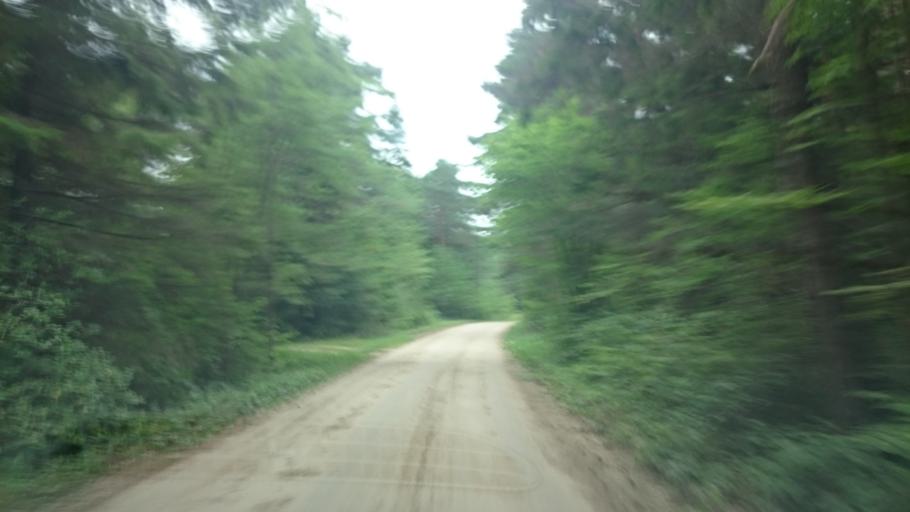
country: EE
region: Saare
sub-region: Orissaare vald
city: Orissaare
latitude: 58.5903
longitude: 22.7047
